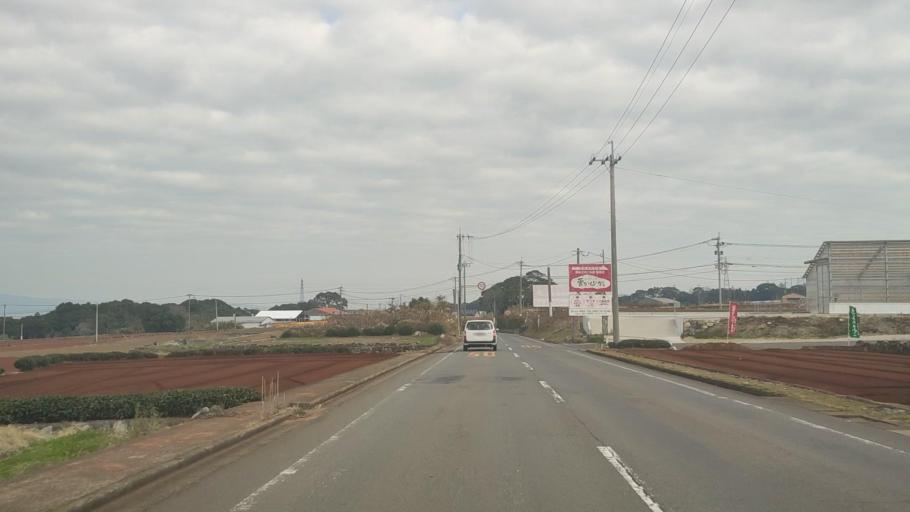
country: JP
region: Nagasaki
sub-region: Isahaya-shi
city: Isahaya
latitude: 32.7997
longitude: 130.1650
